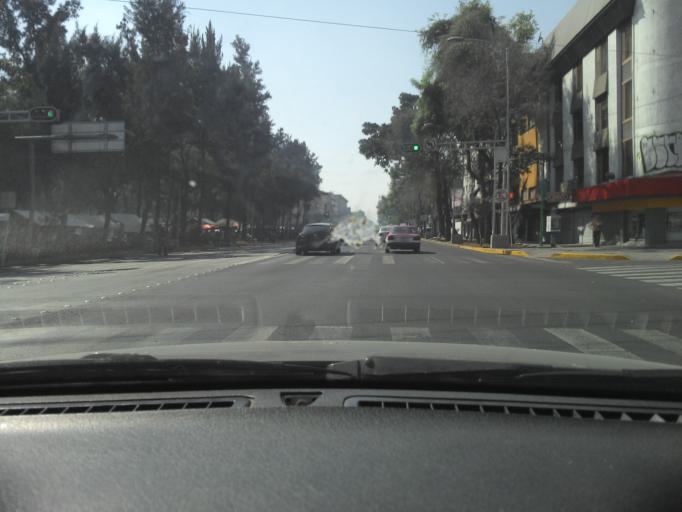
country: MX
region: Mexico City
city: Cuauhtemoc
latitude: 19.4227
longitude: -99.1540
